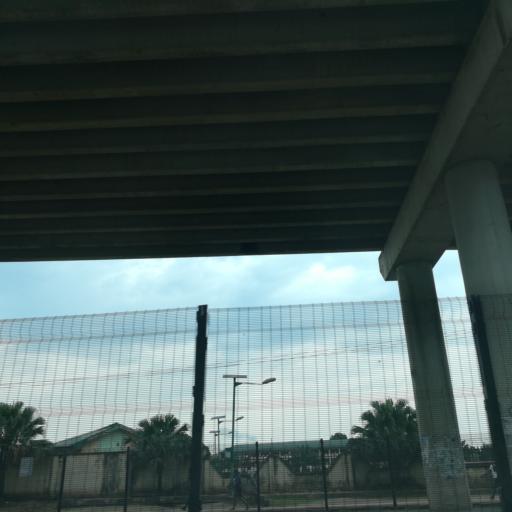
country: NG
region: Rivers
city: Port Harcourt
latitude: 4.8144
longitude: 6.9839
